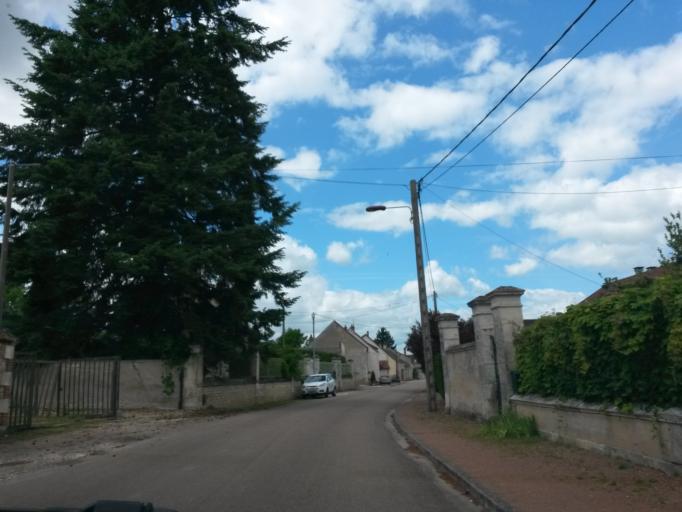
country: FR
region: Centre
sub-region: Departement du Cher
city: Herry
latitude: 47.2421
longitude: 2.9979
